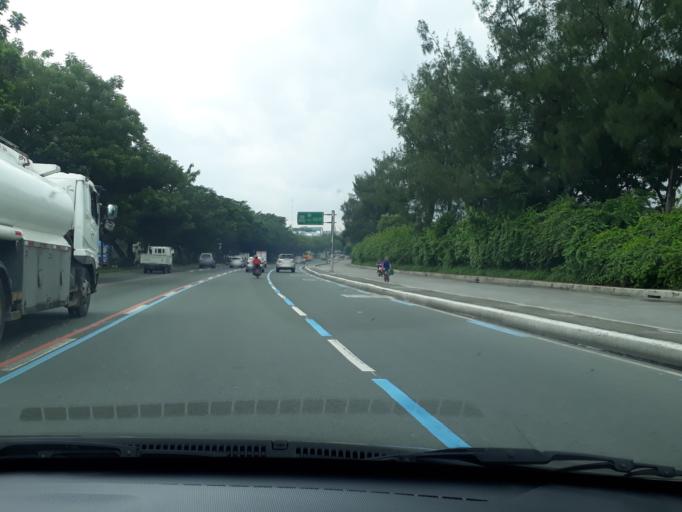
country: PH
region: Calabarzon
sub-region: Province of Rizal
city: Taguig
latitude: 14.5217
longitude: 121.0539
